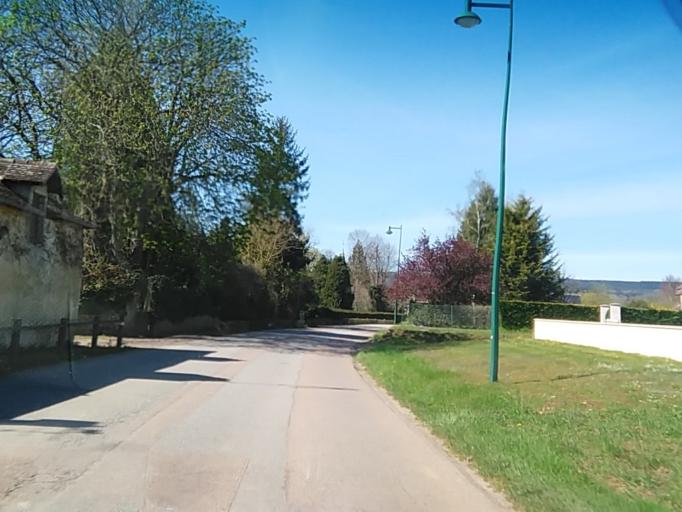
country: FR
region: Lower Normandy
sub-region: Departement de l'Orne
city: Conde-sur-Sarthe
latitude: 48.4679
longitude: 0.0181
